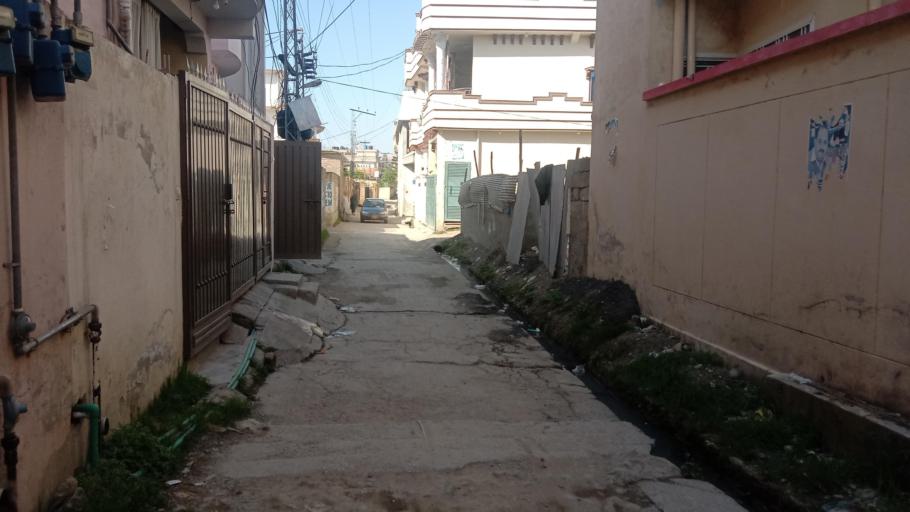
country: PK
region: Khyber Pakhtunkhwa
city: Abbottabad
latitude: 34.1776
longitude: 73.2252
